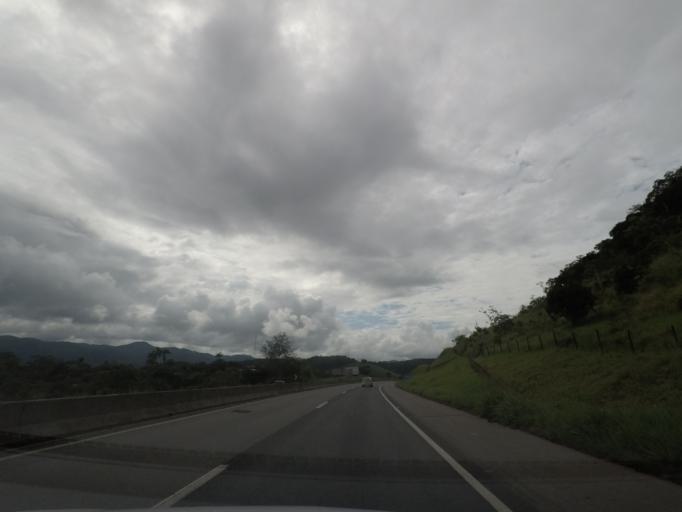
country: BR
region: Sao Paulo
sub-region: Miracatu
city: Miracatu
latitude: -24.2047
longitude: -47.3721
